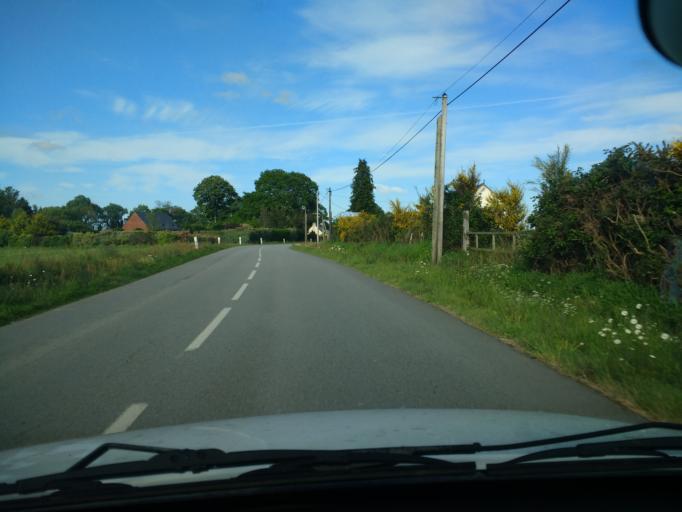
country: FR
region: Brittany
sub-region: Departement du Morbihan
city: Pluherlin
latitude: 47.6991
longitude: -2.3781
